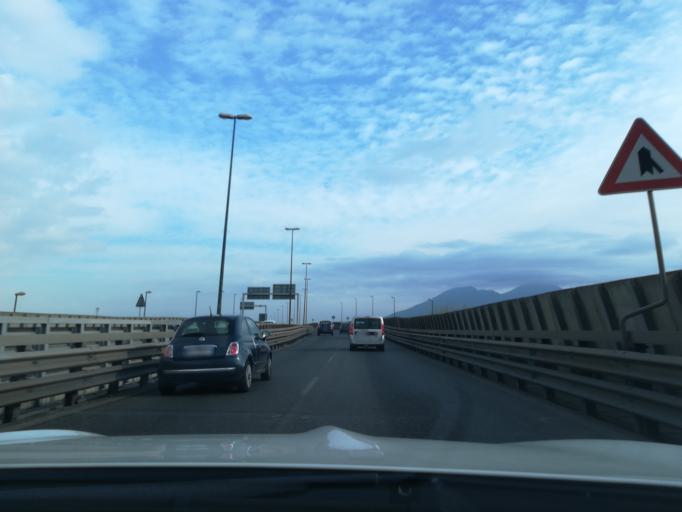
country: IT
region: Campania
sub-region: Provincia di Napoli
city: Arpino
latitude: 40.8638
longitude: 14.2927
